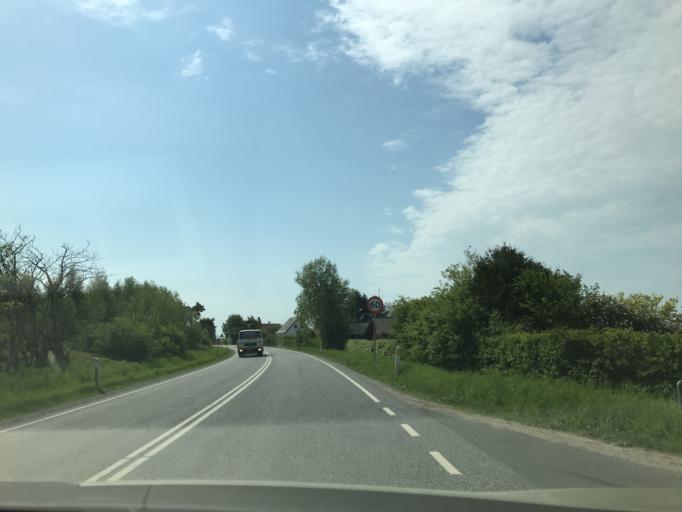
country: DK
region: South Denmark
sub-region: Middelfart Kommune
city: Ejby
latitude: 55.3778
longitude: 9.9170
